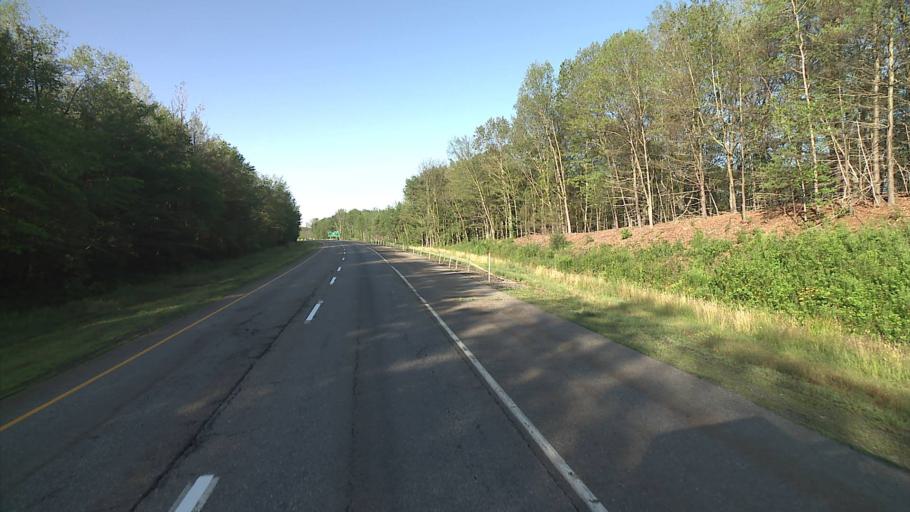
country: US
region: Connecticut
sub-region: Windham County
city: Thompson
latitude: 41.9714
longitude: -71.8690
